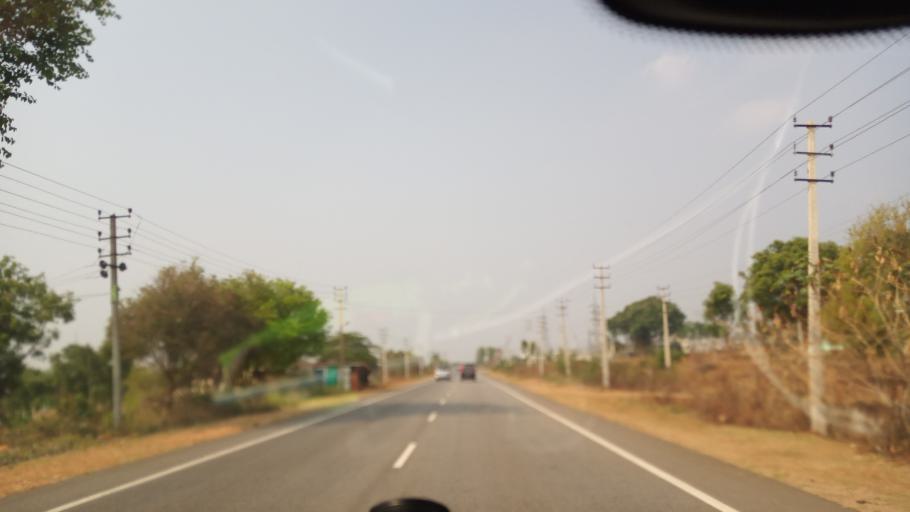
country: IN
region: Karnataka
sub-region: Mandya
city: Melukote
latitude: 12.7246
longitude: 76.7131
